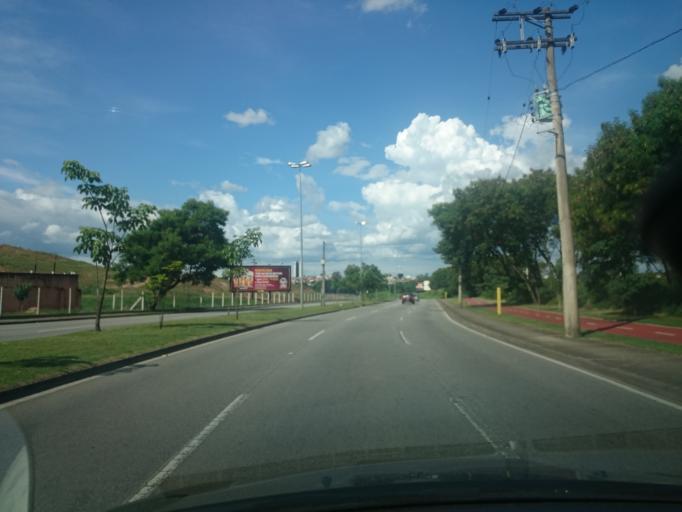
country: BR
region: Sao Paulo
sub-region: Sorocaba
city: Sorocaba
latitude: -23.5186
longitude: -47.4525
